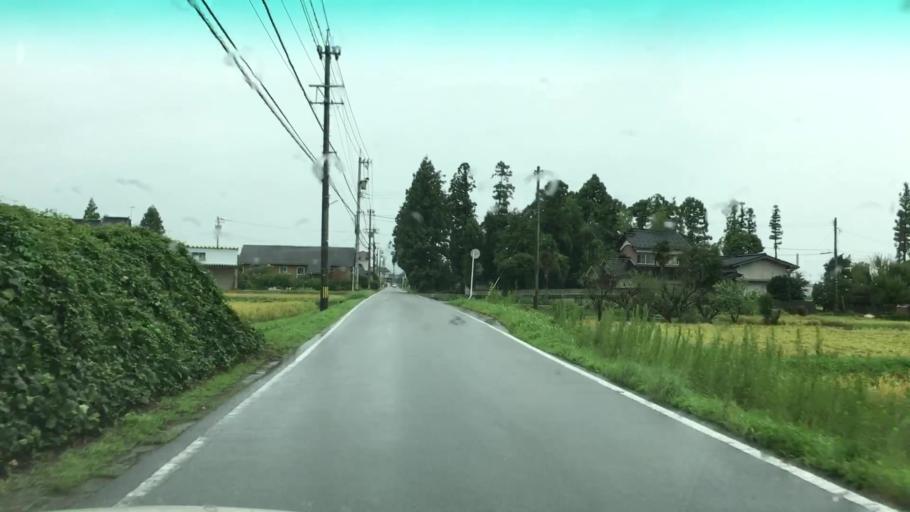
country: JP
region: Toyama
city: Kamiichi
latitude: 36.6743
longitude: 137.3209
